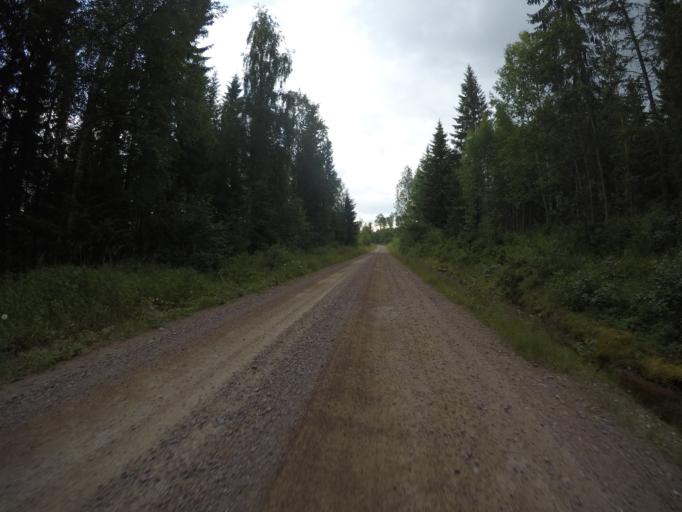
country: SE
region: Vaermland
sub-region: Filipstads Kommun
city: Lesjofors
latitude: 60.1953
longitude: 14.3939
